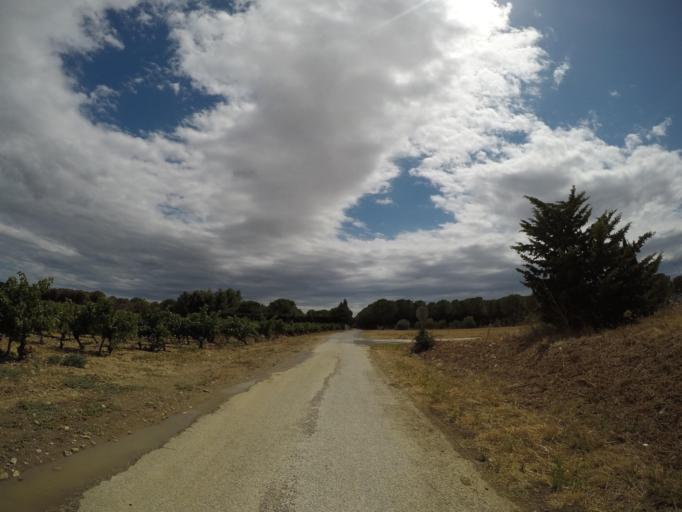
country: FR
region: Languedoc-Roussillon
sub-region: Departement des Pyrenees-Orientales
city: Baho
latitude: 42.7108
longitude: 2.8172
